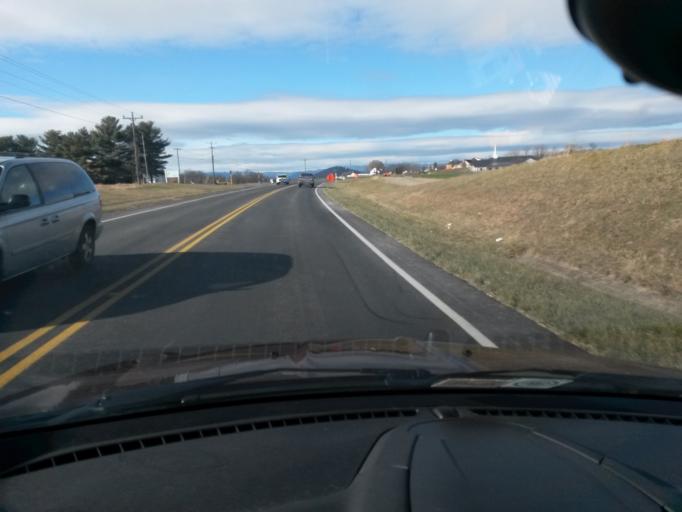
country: US
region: Virginia
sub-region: Rockingham County
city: Bridgewater
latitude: 38.3674
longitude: -78.9459
